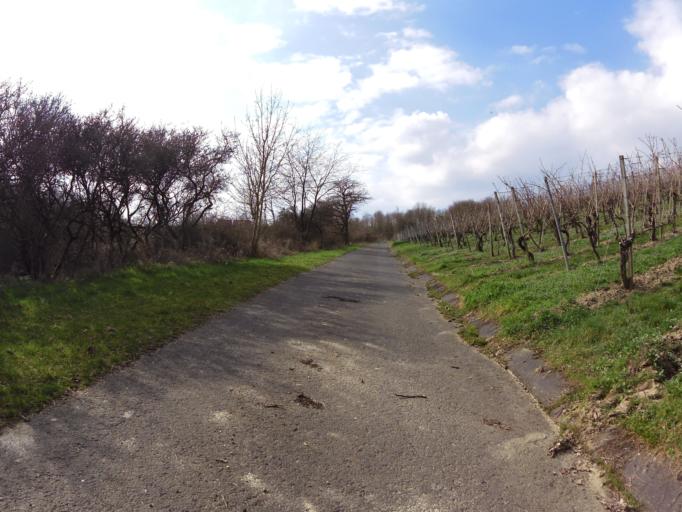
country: DE
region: Bavaria
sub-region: Regierungsbezirk Unterfranken
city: Buchbrunn
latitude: 49.7359
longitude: 10.1090
